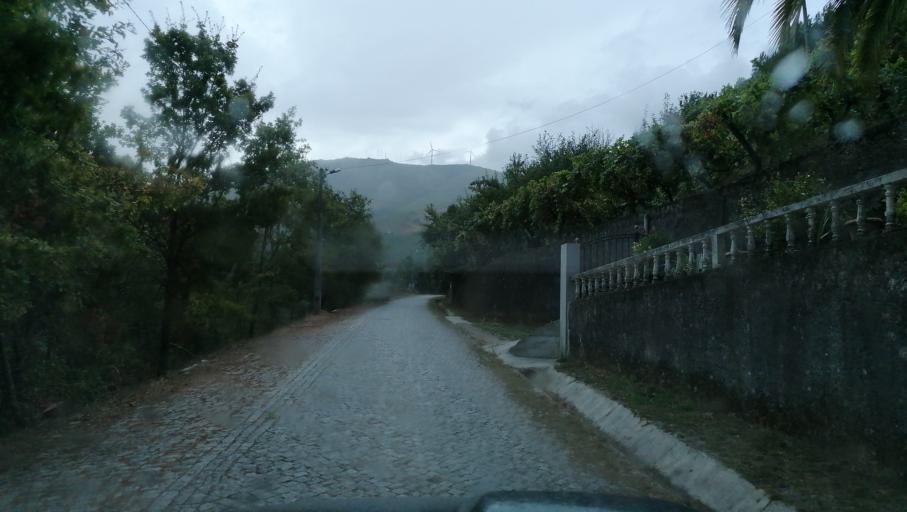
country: PT
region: Vila Real
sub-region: Vila Pouca de Aguiar
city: Vila Pouca de Aguiar
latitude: 41.5602
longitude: -7.7147
